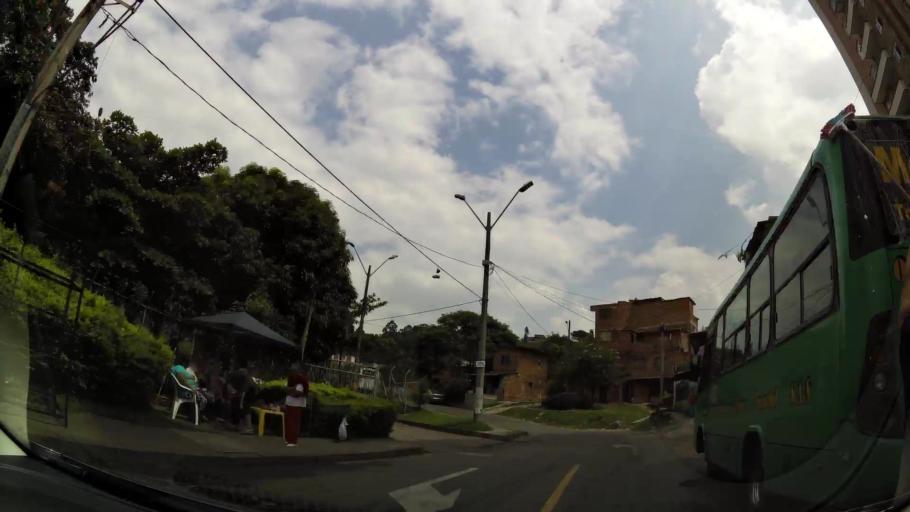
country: CO
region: Antioquia
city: Itagui
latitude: 6.1967
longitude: -75.5952
